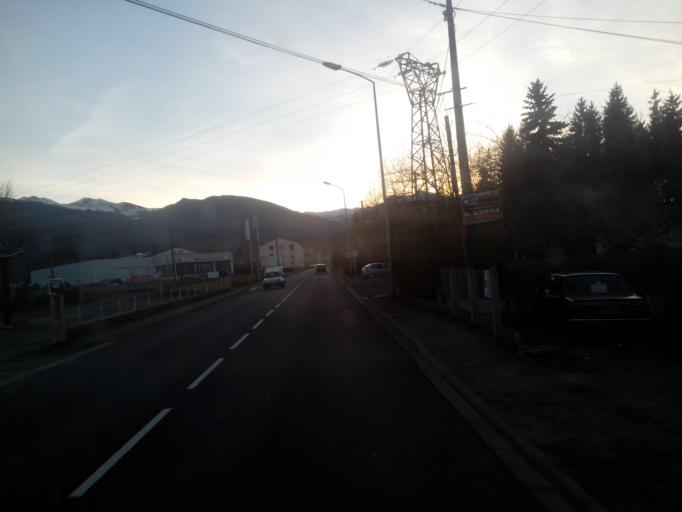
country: FR
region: Midi-Pyrenees
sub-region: Departement de l'Ariege
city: Lavelanet
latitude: 42.9217
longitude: 1.8336
